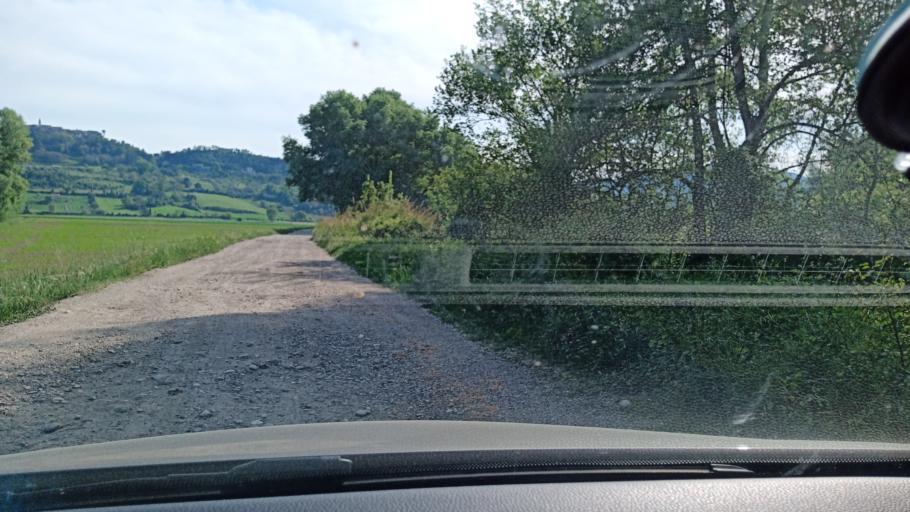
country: IT
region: Latium
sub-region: Citta metropolitana di Roma Capitale
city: Ponzano Romano
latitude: 42.2732
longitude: 12.5764
